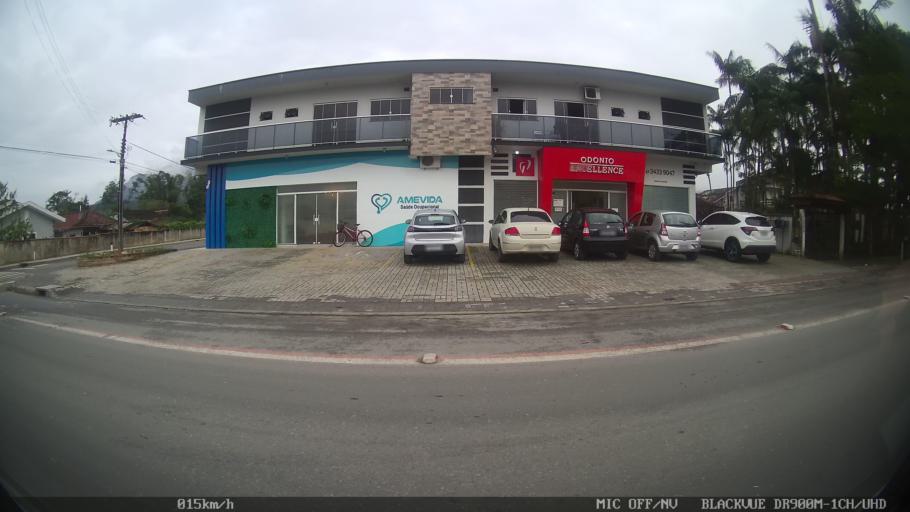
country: BR
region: Santa Catarina
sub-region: Joinville
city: Joinville
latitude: -26.0380
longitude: -48.8567
